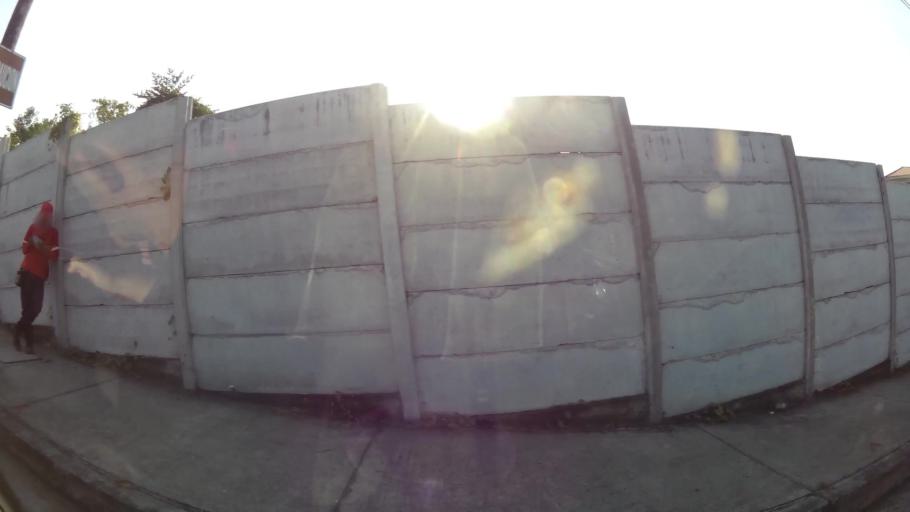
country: EC
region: Guayas
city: Guayaquil
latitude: -2.1553
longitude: -79.9051
